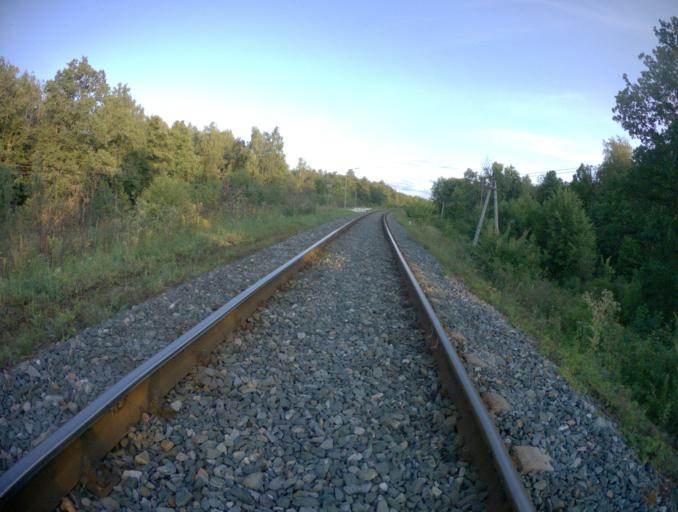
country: RU
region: Vladimir
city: Raduzhnyy
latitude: 56.0436
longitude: 40.3841
